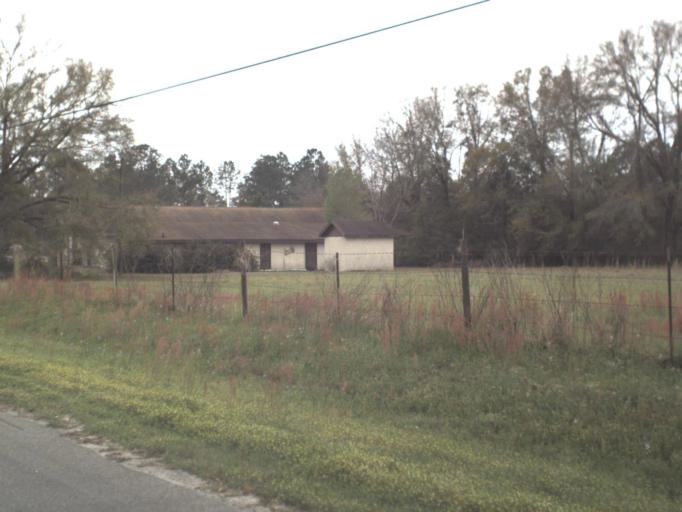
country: US
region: Florida
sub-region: Gulf County
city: Wewahitchka
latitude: 30.0909
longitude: -85.1954
